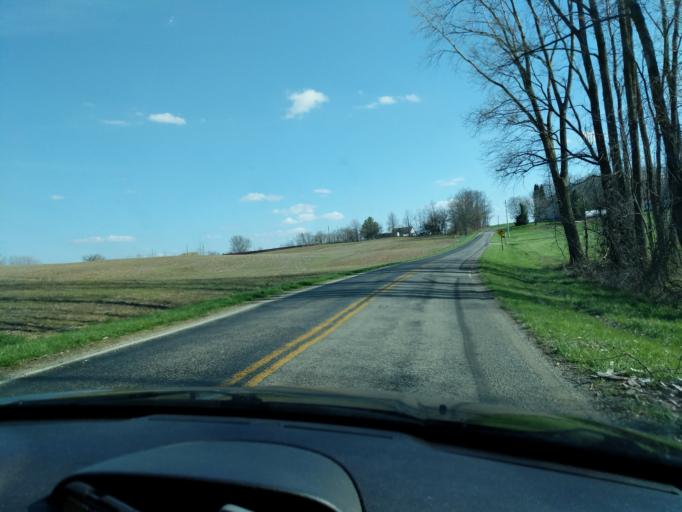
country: US
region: Ohio
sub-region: Logan County
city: De Graff
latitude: 40.2600
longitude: -83.8698
